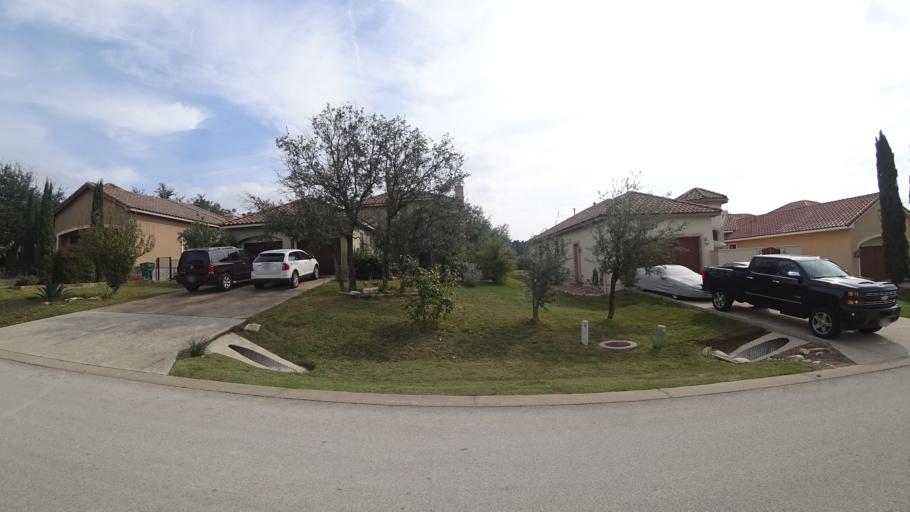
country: US
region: Texas
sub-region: Travis County
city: Hudson Bend
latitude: 30.3863
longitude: -97.9298
